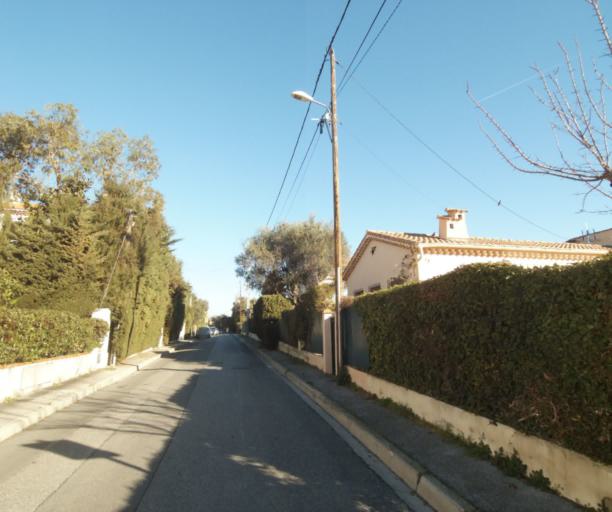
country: FR
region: Provence-Alpes-Cote d'Azur
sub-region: Departement des Alpes-Maritimes
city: Antibes
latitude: 43.5810
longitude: 7.1025
